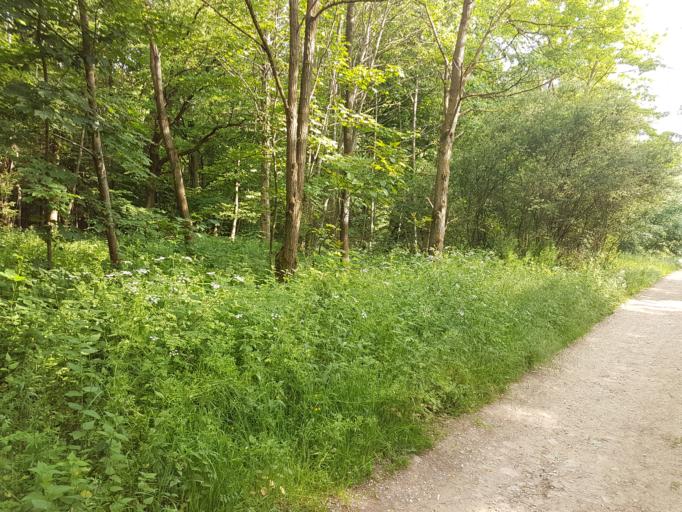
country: LU
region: Luxembourg
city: Itzig
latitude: 49.6099
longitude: 6.1756
